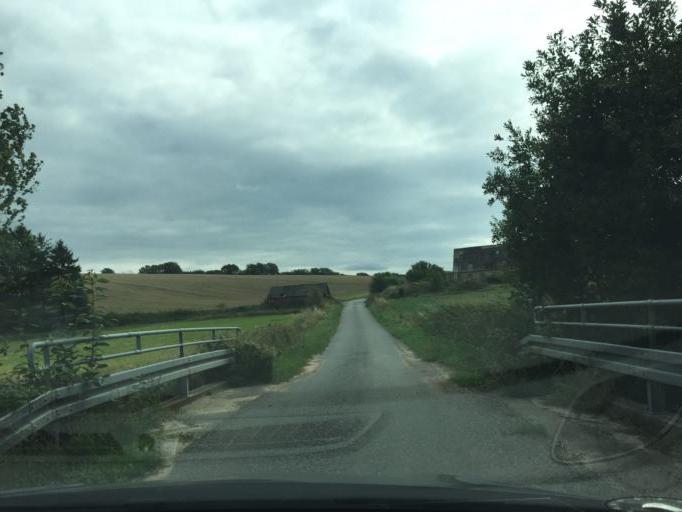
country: DK
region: South Denmark
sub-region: Assens Kommune
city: Vissenbjerg
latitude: 55.3562
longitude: 10.1173
